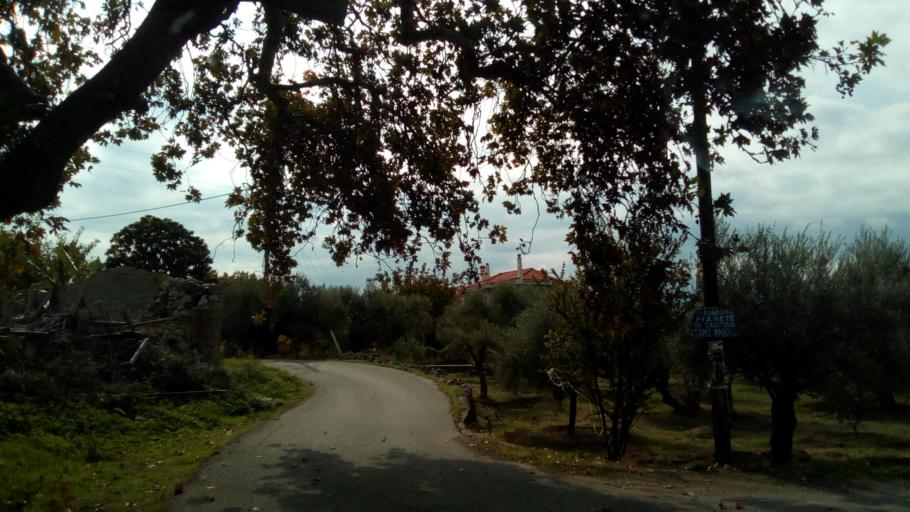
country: GR
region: West Greece
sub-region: Nomos Achaias
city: Kamarai
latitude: 38.3939
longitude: 22.0563
